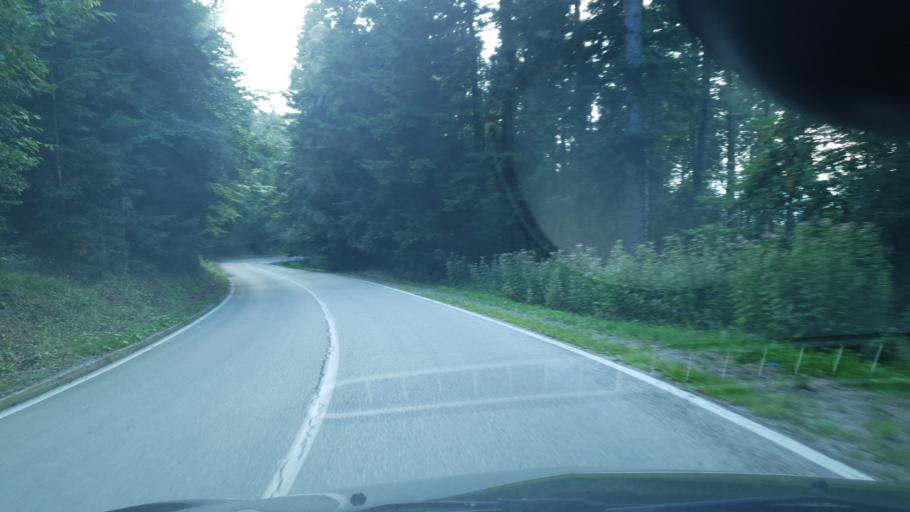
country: HR
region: Grad Zagreb
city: Kasina
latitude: 45.9193
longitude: 15.9726
